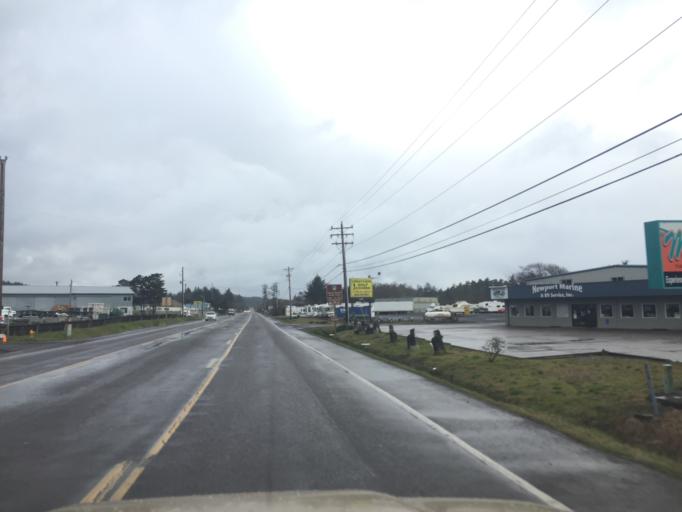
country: US
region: Oregon
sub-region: Lincoln County
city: Newport
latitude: 44.6068
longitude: -124.0538
